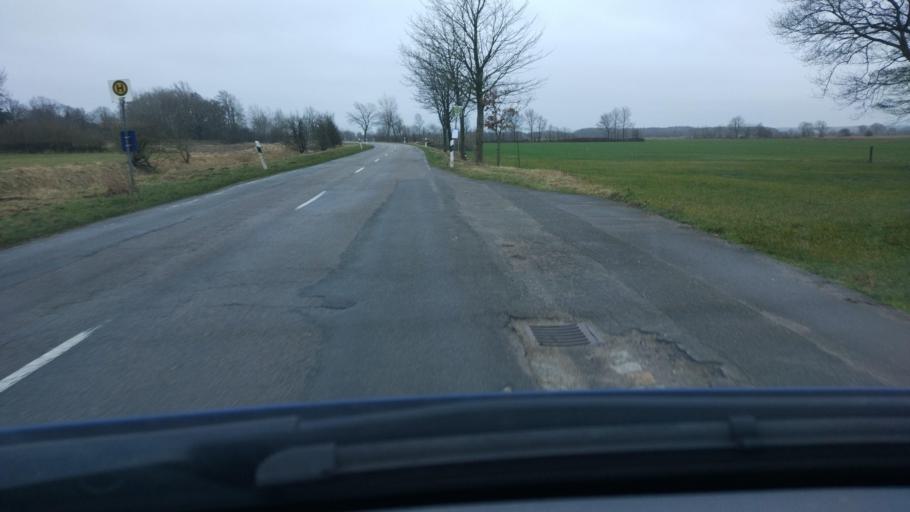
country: DE
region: Schleswig-Holstein
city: Treia
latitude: 54.4899
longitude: 9.3439
